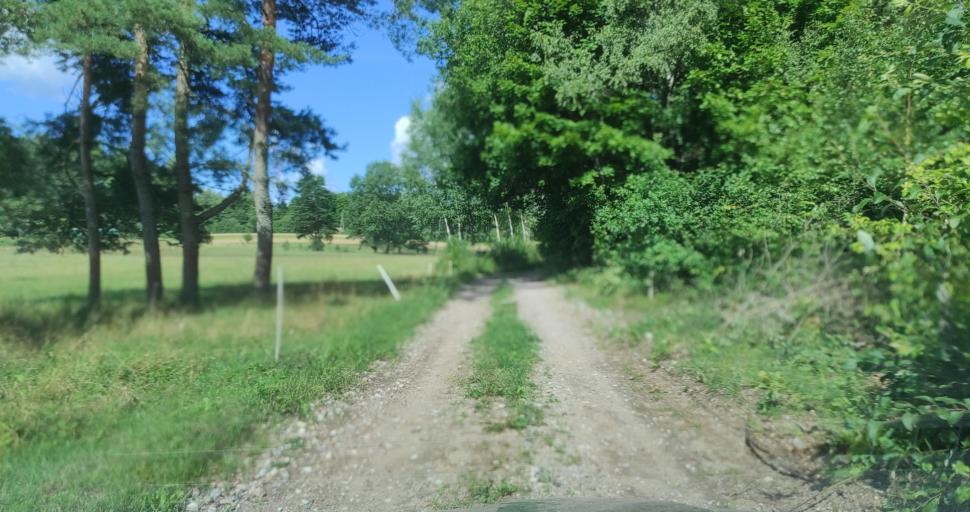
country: LV
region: Alsunga
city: Alsunga
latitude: 57.0259
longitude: 21.7028
